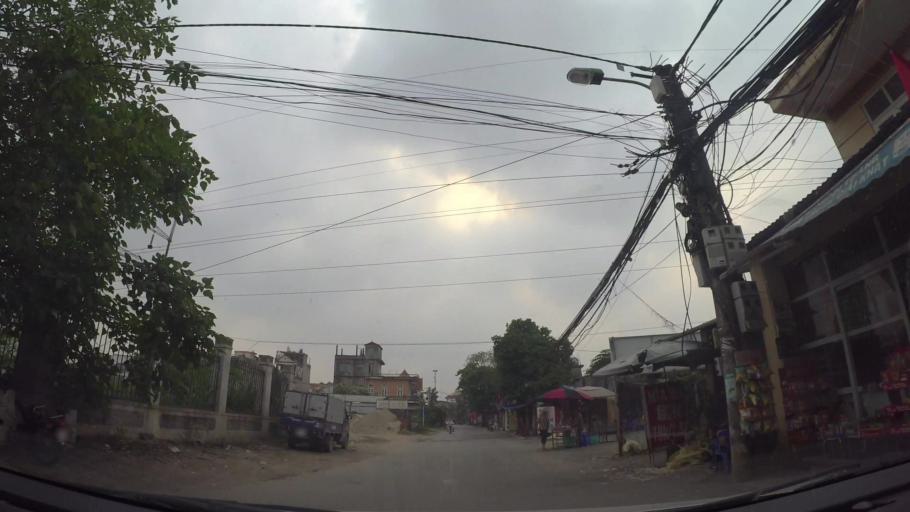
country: VN
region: Ha Noi
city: Cau Dien
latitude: 21.0349
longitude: 105.7479
